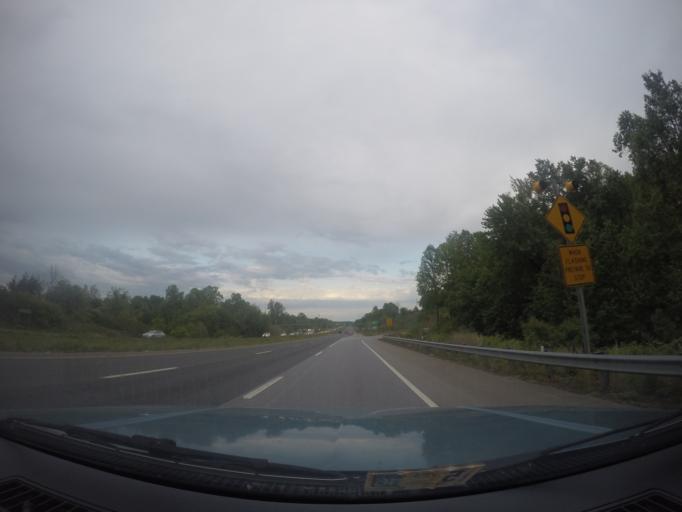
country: US
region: Virginia
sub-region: City of Lynchburg
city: Lynchburg
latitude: 37.3862
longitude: -79.1026
